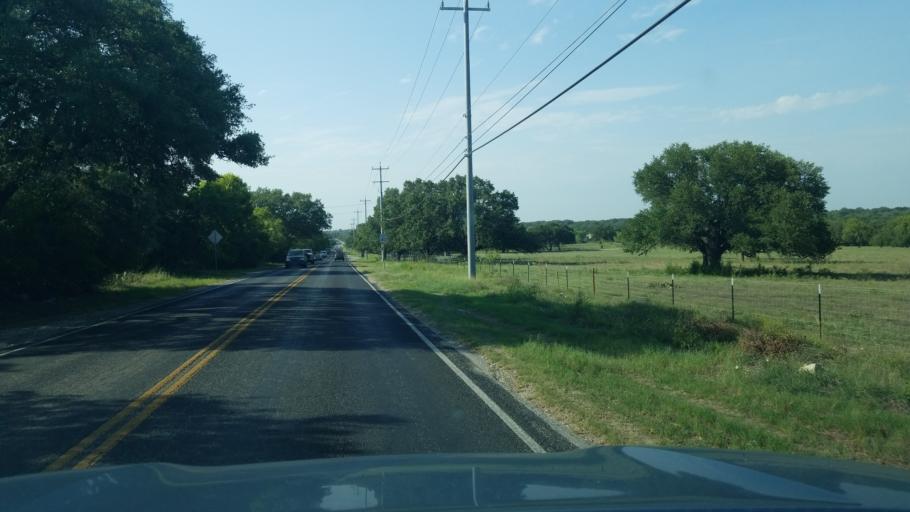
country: US
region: Texas
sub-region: Bexar County
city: Helotes
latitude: 29.4536
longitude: -98.7552
